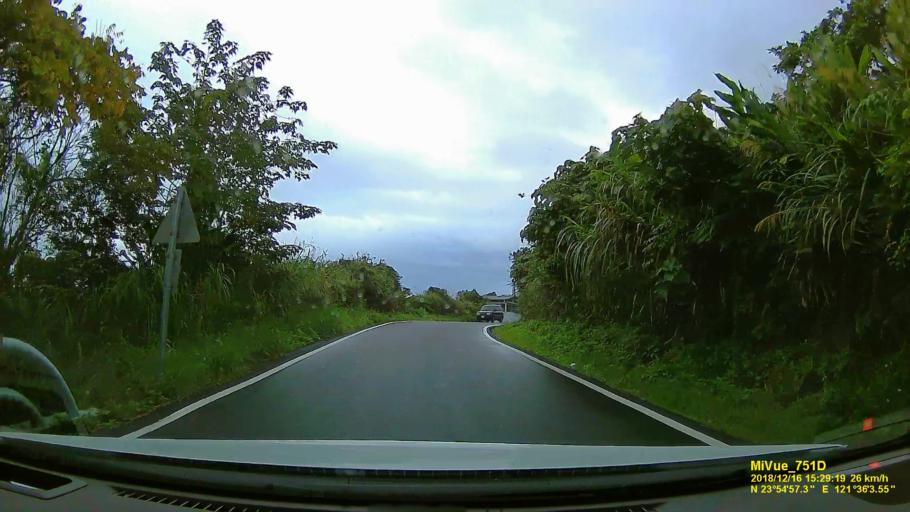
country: TW
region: Taiwan
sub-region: Hualien
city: Hualian
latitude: 23.9156
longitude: 121.6010
